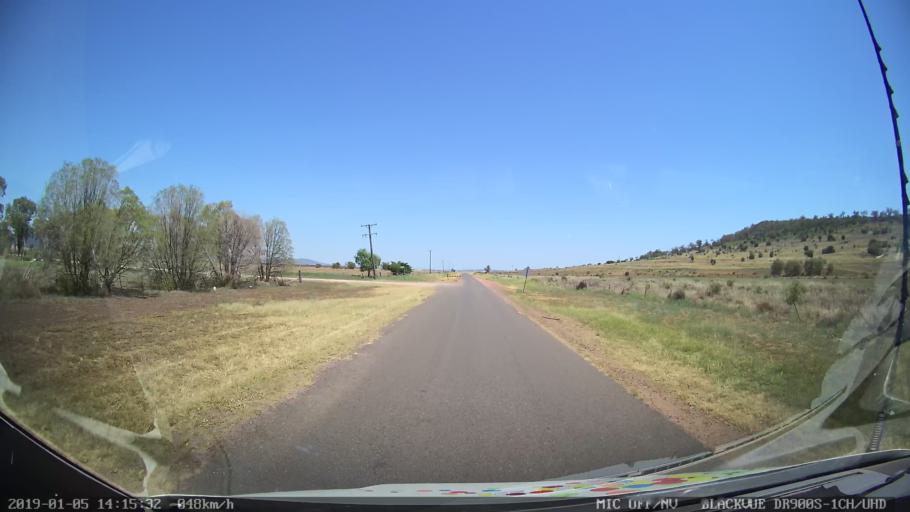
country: AU
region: New South Wales
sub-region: Liverpool Plains
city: Quirindi
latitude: -31.2483
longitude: 150.4712
